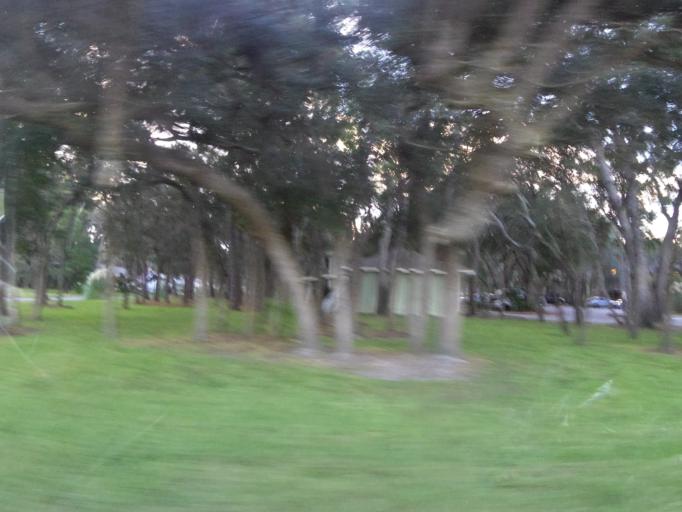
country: US
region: Georgia
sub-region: Camden County
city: St. Marys
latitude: 30.7351
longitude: -81.5542
